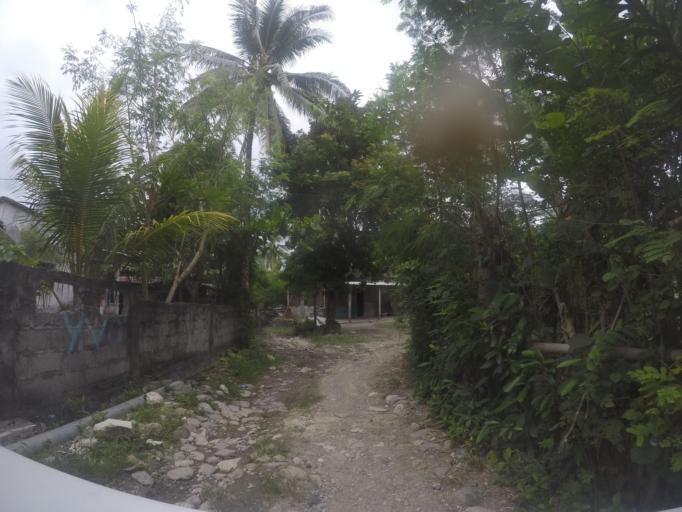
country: TL
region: Viqueque
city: Viqueque
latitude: -8.8660
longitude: 126.3651
